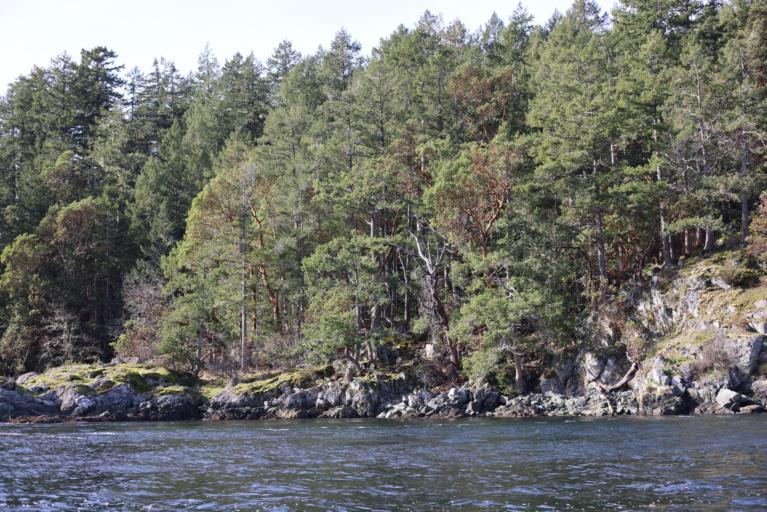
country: CA
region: British Columbia
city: North Cowichan
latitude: 48.7814
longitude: -123.5573
